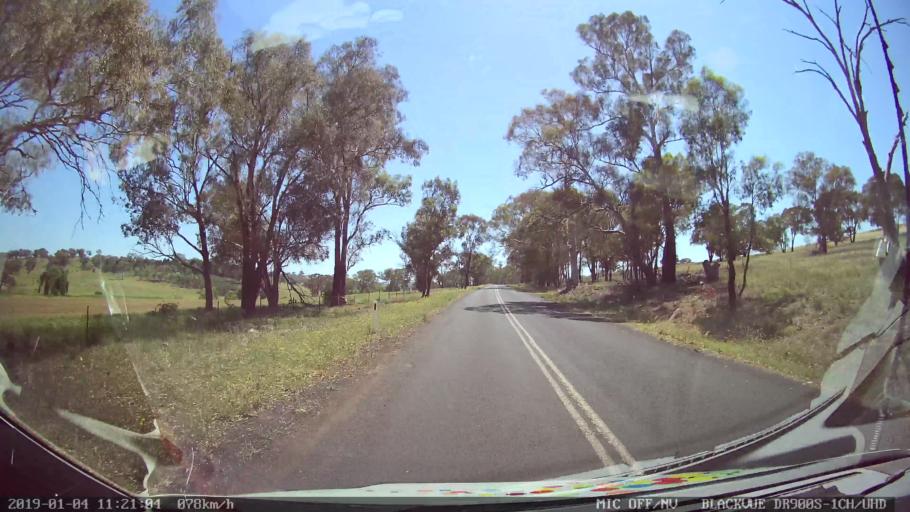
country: AU
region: New South Wales
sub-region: Cabonne
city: Molong
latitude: -33.1573
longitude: 148.7069
